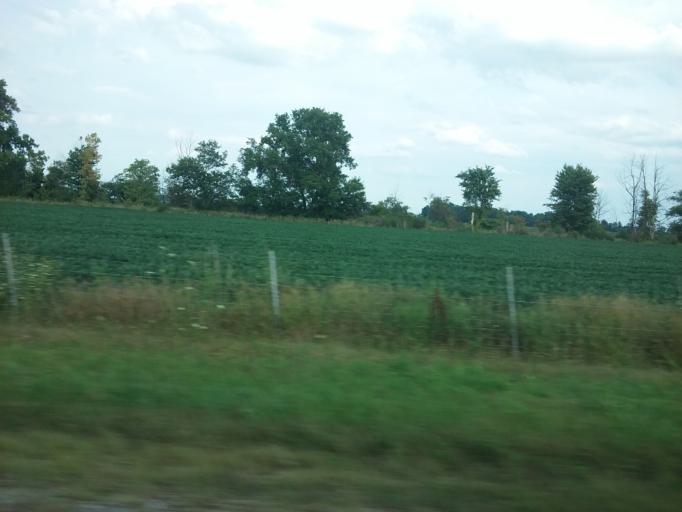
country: US
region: Ohio
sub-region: Wood County
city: Bowling Green
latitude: 41.2955
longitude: -83.6503
